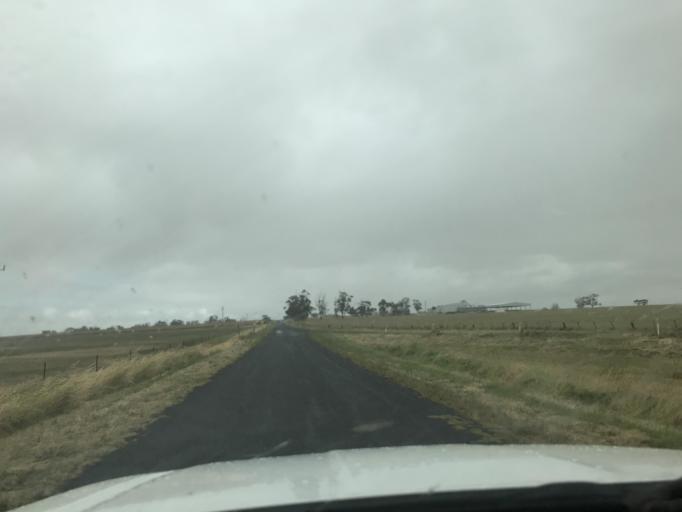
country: AU
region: South Australia
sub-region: Tatiara
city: Bordertown
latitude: -36.3120
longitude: 141.1438
